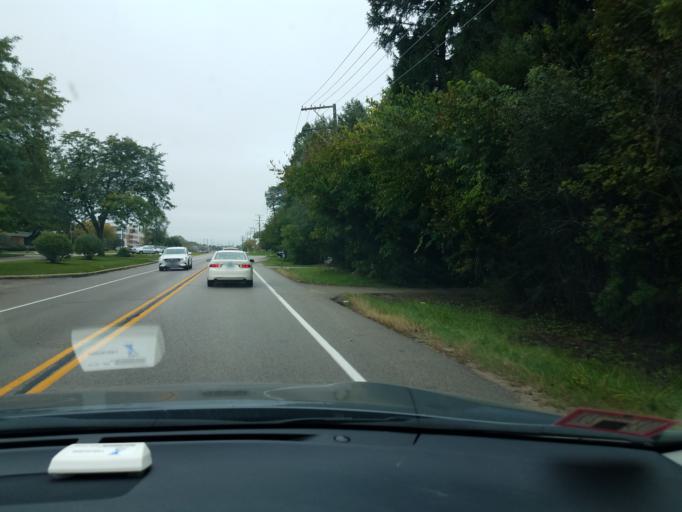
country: US
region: Illinois
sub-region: Lake County
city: Riverwoods
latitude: 42.1677
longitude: -87.9162
